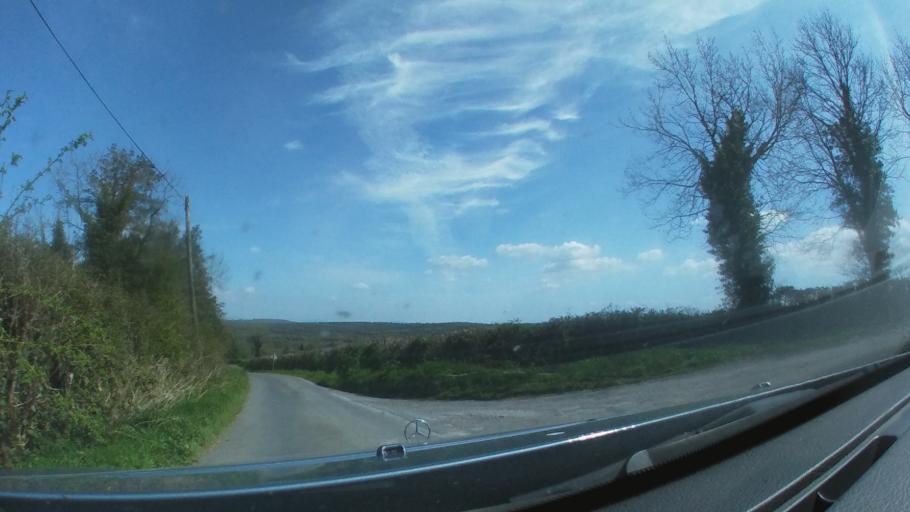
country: IE
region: Leinster
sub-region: Kilkenny
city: Callan
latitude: 52.6176
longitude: -7.4946
